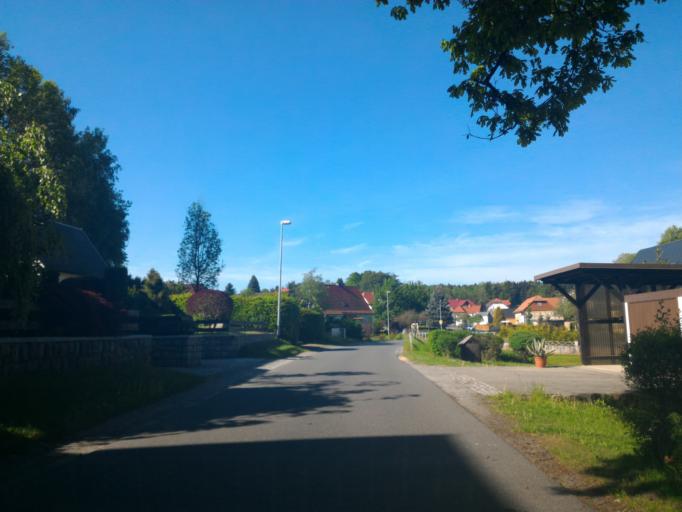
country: DE
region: Saxony
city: Grossschweidnitz
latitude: 51.0638
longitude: 14.6357
